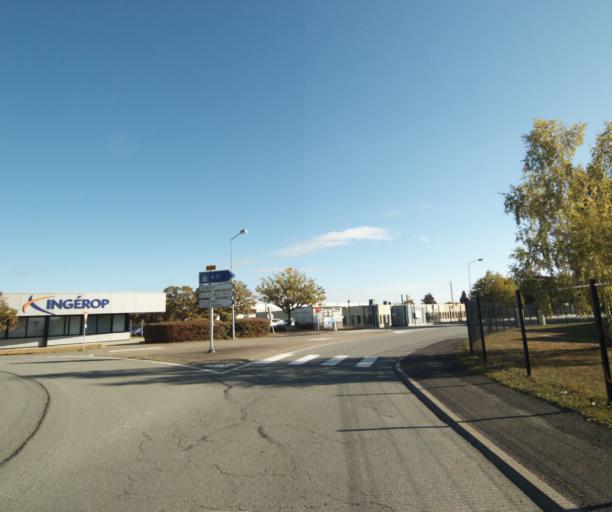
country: FR
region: Auvergne
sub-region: Departement du Puy-de-Dome
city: Cebazat
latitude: 45.8379
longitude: 3.1184
